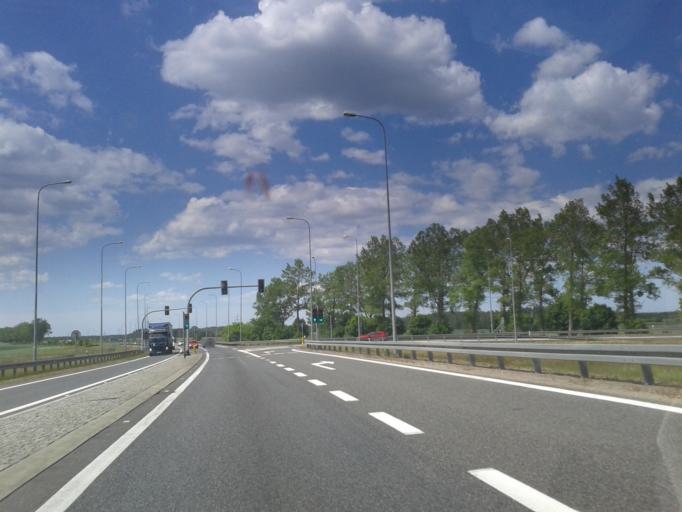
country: PL
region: Pomeranian Voivodeship
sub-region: Powiat chojnicki
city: Chojnice
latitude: 53.6889
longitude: 17.4751
